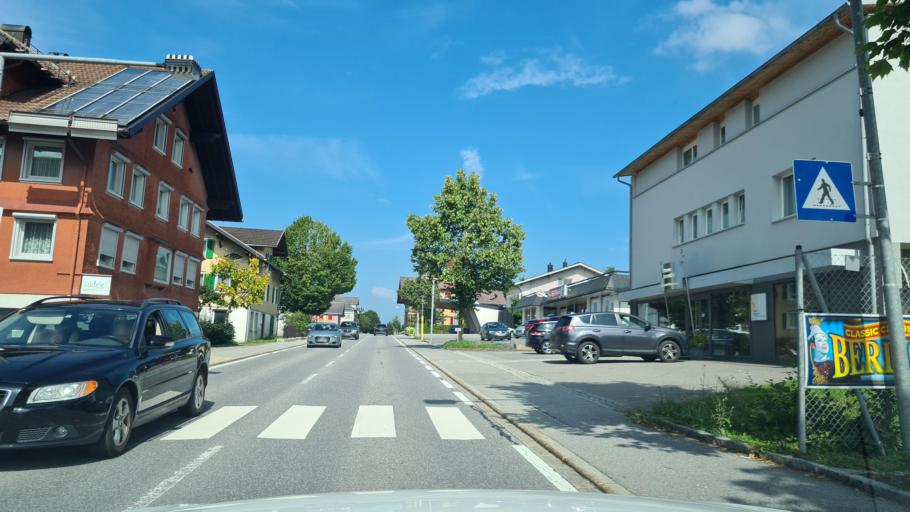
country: AT
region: Vorarlberg
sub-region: Politischer Bezirk Bregenz
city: Doren
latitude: 47.4513
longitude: 9.8346
